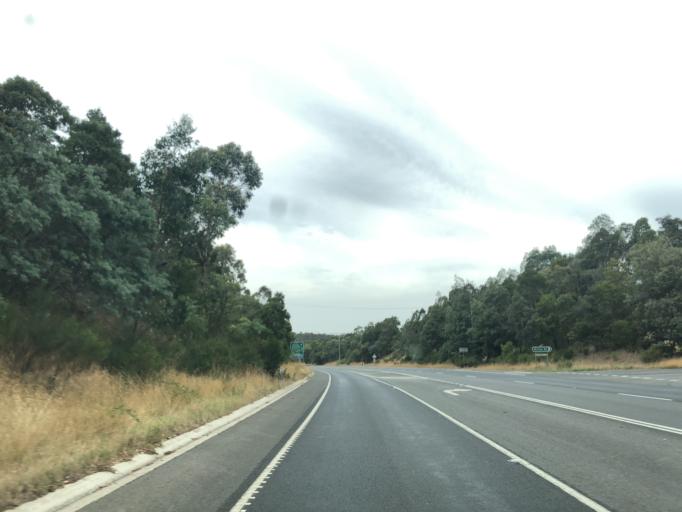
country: AU
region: Victoria
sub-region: Hume
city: Sunbury
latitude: -37.4103
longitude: 144.5404
